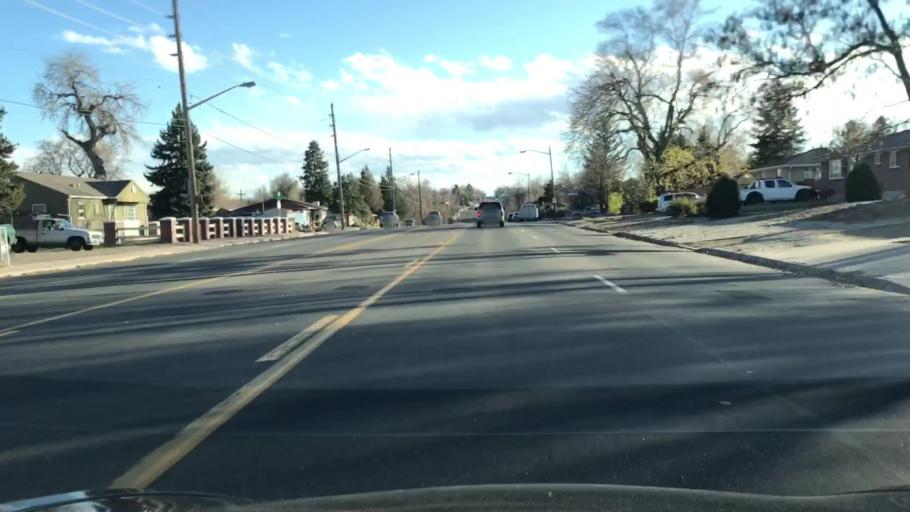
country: US
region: Colorado
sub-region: Jefferson County
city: Lakewood
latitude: 39.6867
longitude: -105.0532
